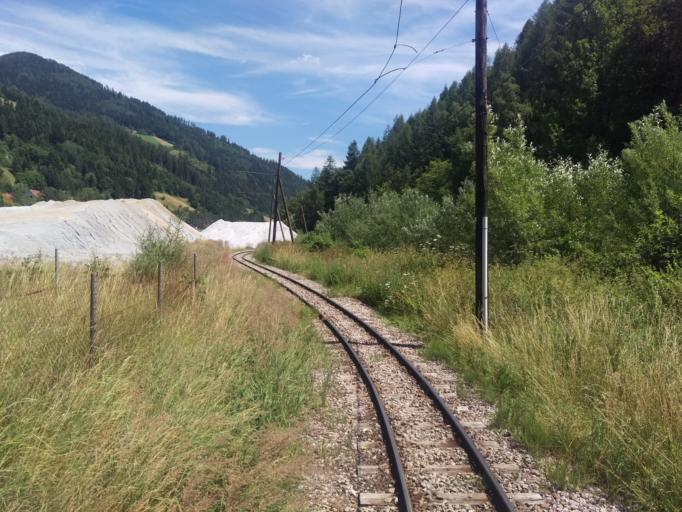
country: AT
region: Styria
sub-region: Politischer Bezirk Bruck-Muerzzuschlag
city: Allerheiligen im Muerztal
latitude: 47.3895
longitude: 15.4304
